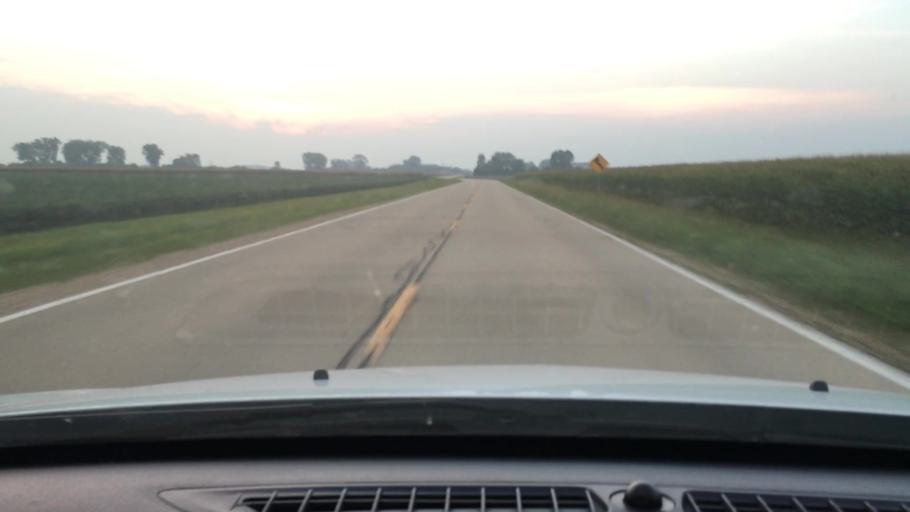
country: US
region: Illinois
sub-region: Ogle County
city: Rochelle
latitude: 41.8475
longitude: -89.0579
